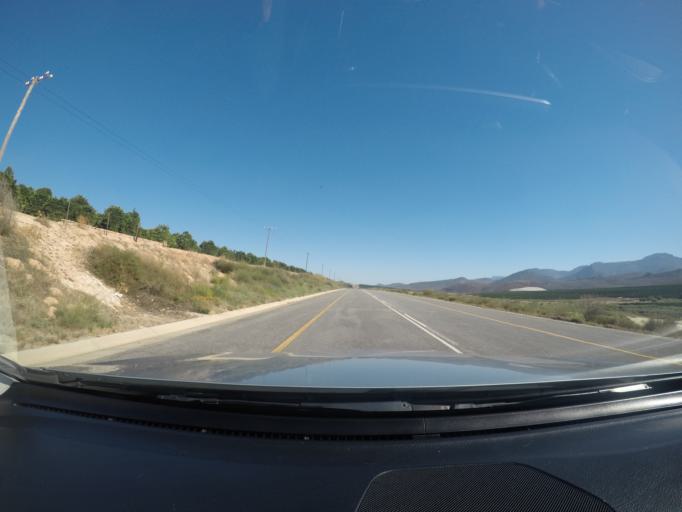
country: ZA
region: Western Cape
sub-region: West Coast District Municipality
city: Clanwilliam
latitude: -32.4896
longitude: 18.9650
